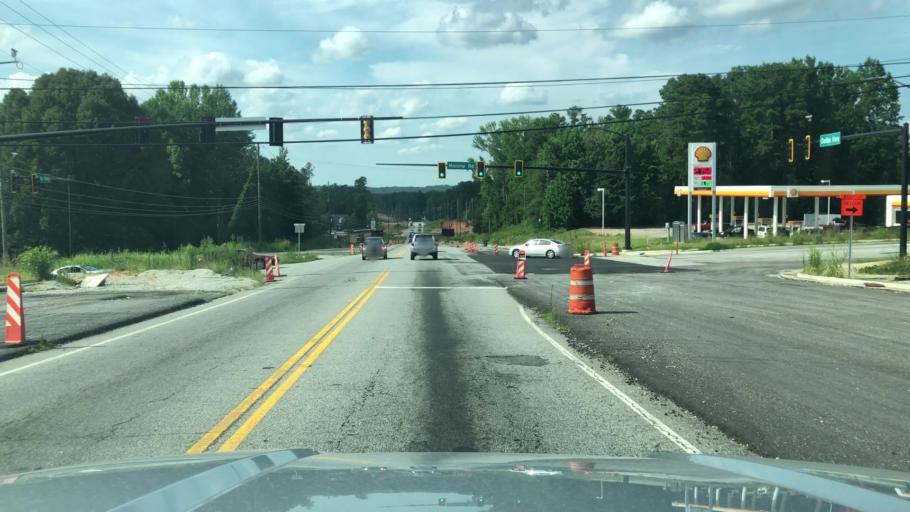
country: US
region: Georgia
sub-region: Douglas County
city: Douglasville
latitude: 33.7696
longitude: -84.7480
